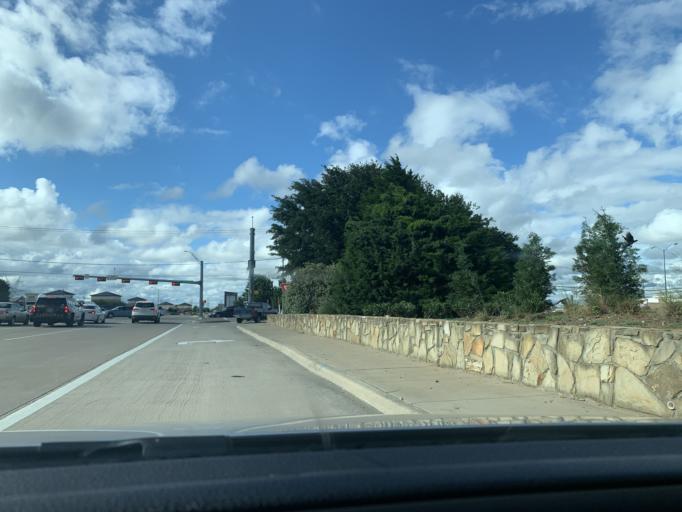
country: US
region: Texas
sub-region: Dallas County
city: Cedar Hill
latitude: 32.6472
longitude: -97.0436
